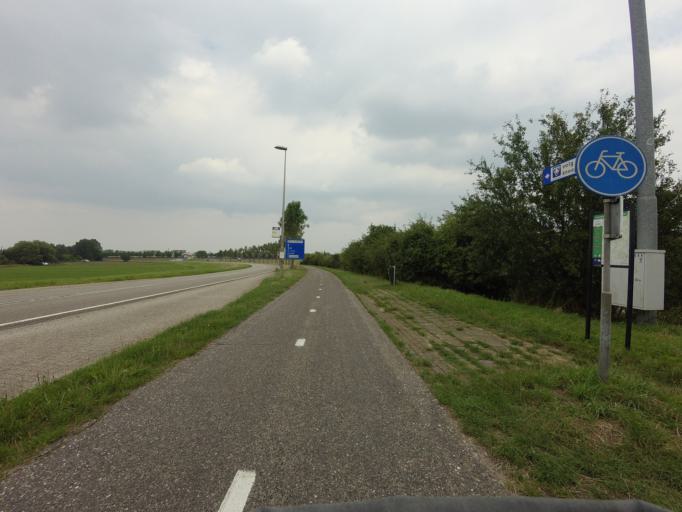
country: NL
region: Utrecht
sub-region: Gemeente Houten
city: Houten
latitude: 52.0074
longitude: 5.1879
